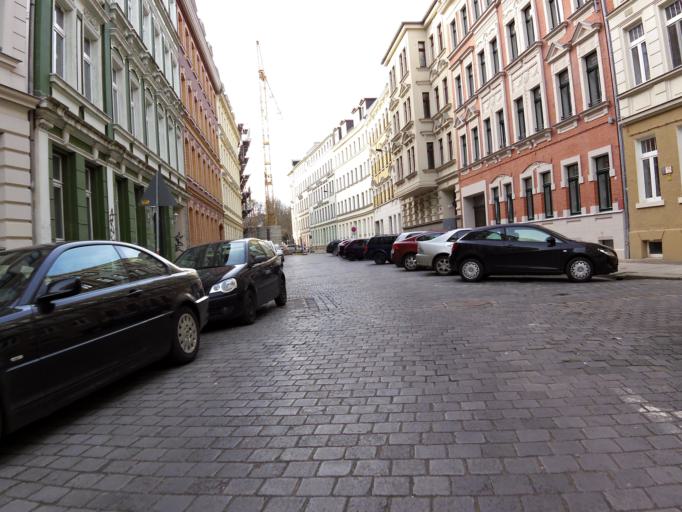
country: DE
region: Saxony
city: Leipzig
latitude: 51.3387
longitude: 12.4058
